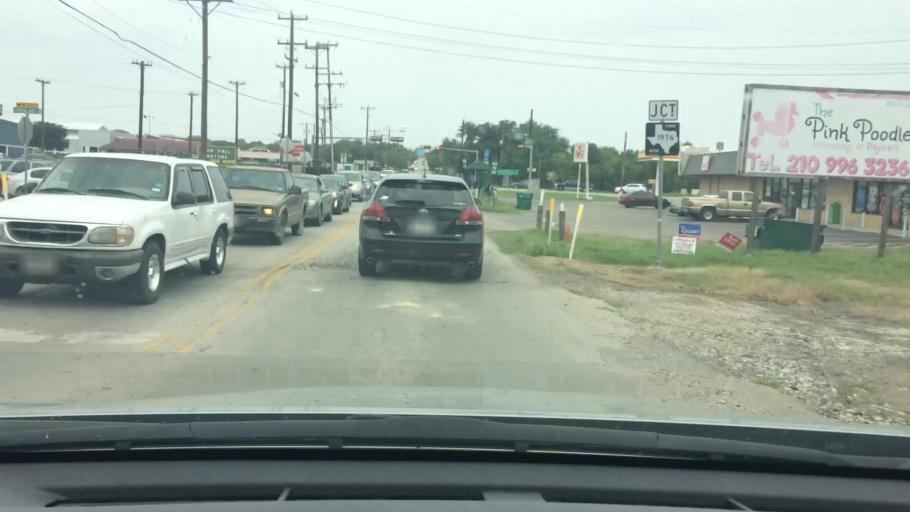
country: US
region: Texas
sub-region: Bexar County
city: Converse
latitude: 29.5175
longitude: -98.3153
